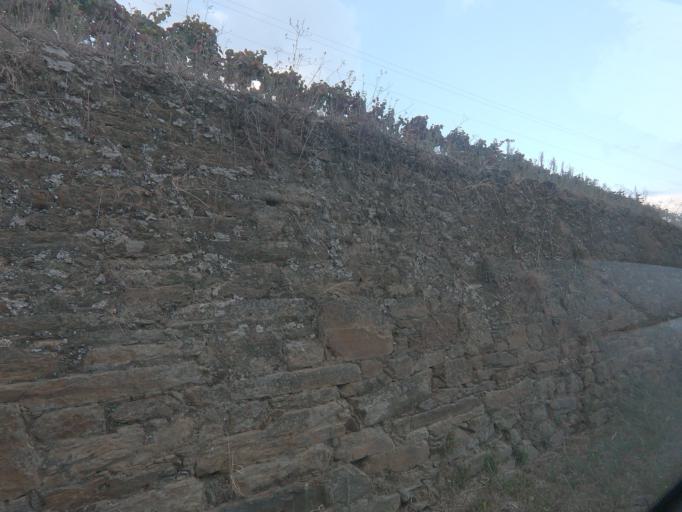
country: PT
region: Vila Real
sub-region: Mesao Frio
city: Mesao Frio
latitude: 41.1787
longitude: -7.8609
